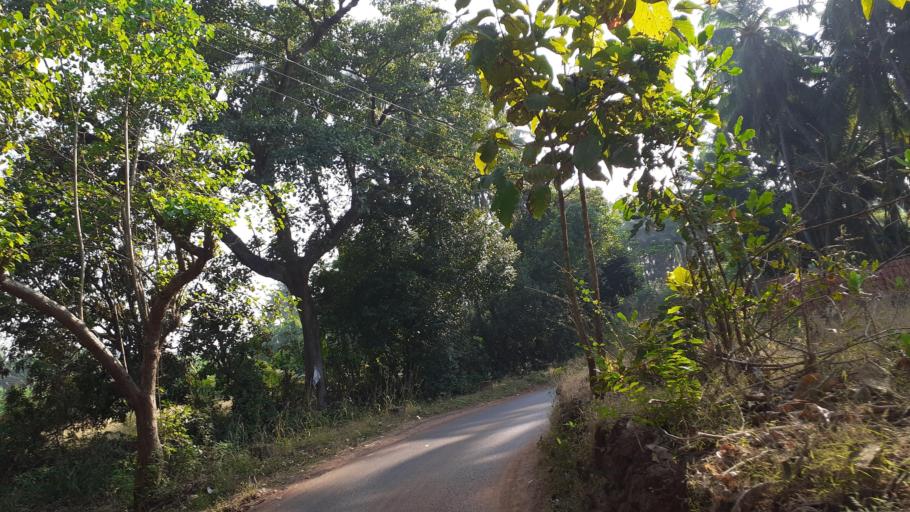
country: IN
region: Maharashtra
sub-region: Ratnagiri
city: Ratnagiri
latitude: 17.2140
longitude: 73.2483
